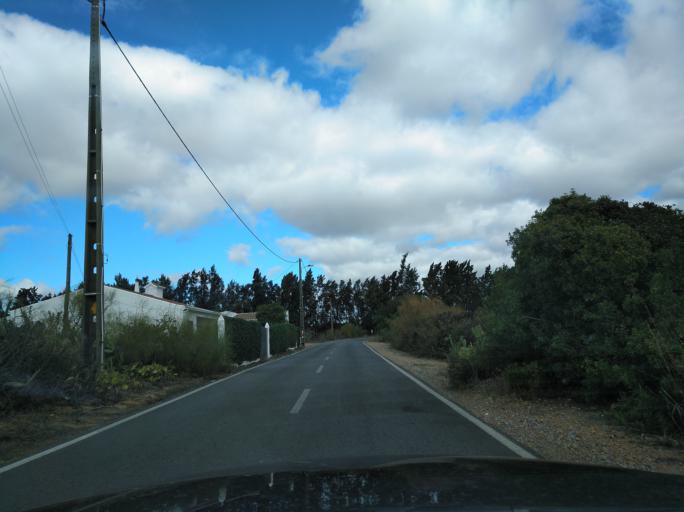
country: PT
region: Faro
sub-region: Vila Real de Santo Antonio
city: Monte Gordo
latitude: 37.1847
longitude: -7.4948
